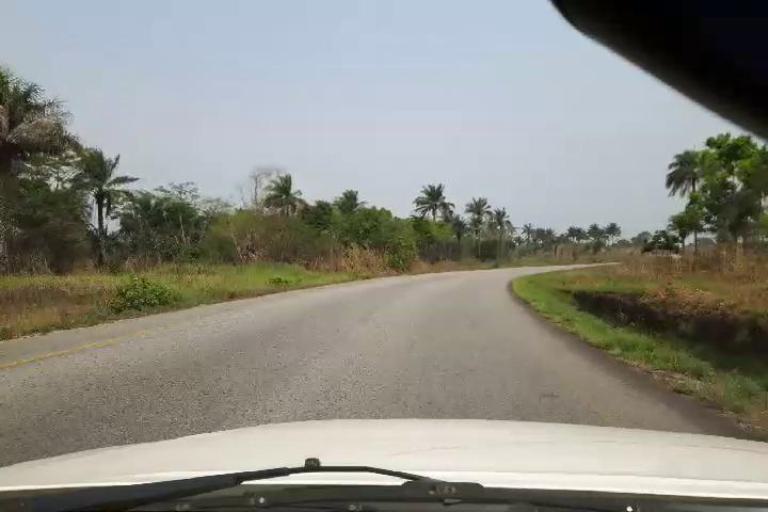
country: SL
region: Southern Province
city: Largo
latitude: 8.3042
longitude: -12.2027
